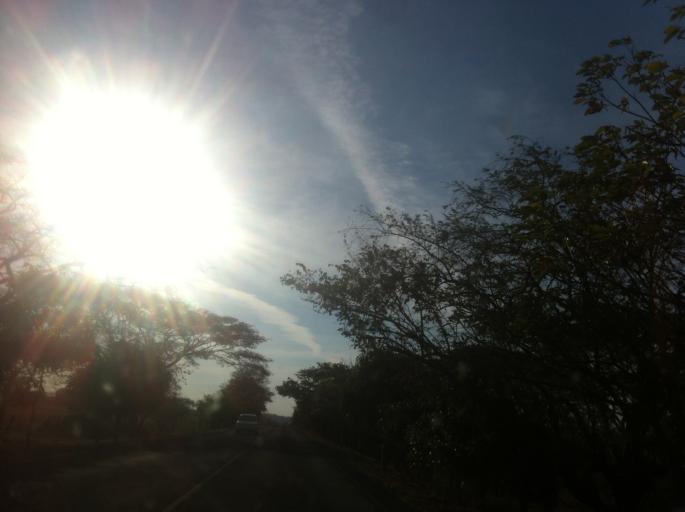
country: NI
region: Rivas
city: San Juan del Sur
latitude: 11.2991
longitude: -85.6887
